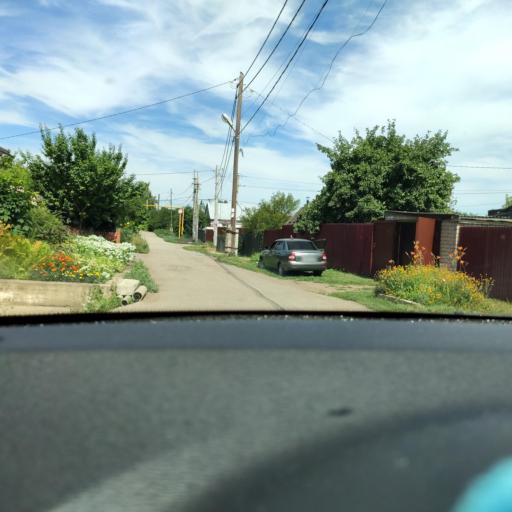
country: RU
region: Samara
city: Smyshlyayevka
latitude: 53.2394
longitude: 50.3413
